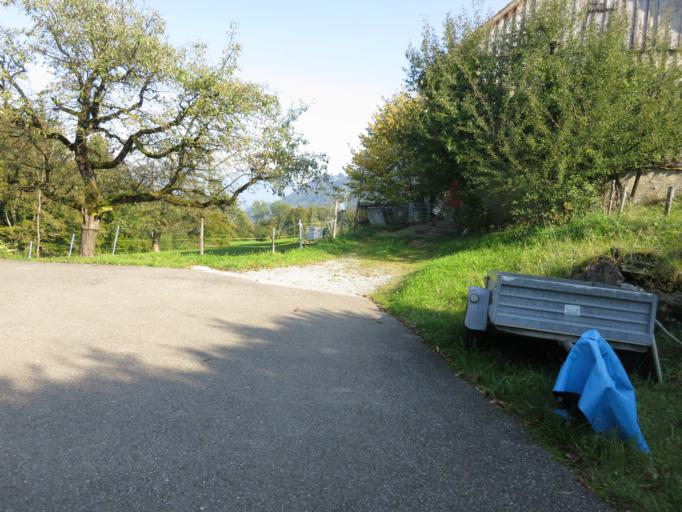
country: CH
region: Schwyz
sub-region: Bezirk March
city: Schubelbach
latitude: 47.1692
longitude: 8.8909
